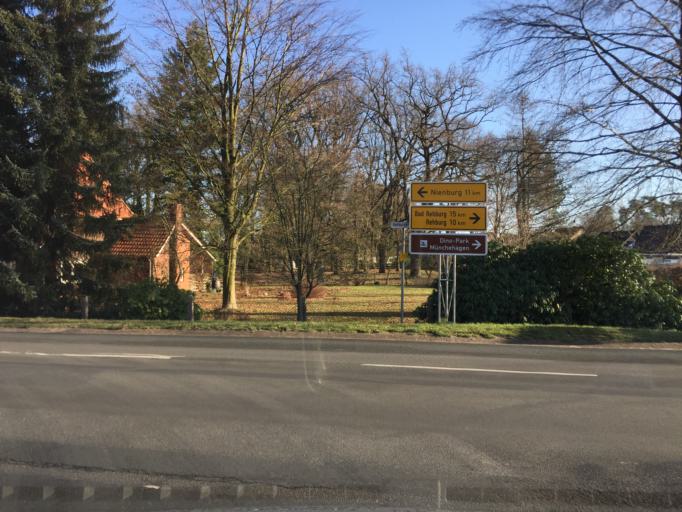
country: DE
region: Lower Saxony
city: Husum
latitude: 52.5638
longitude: 9.2501
